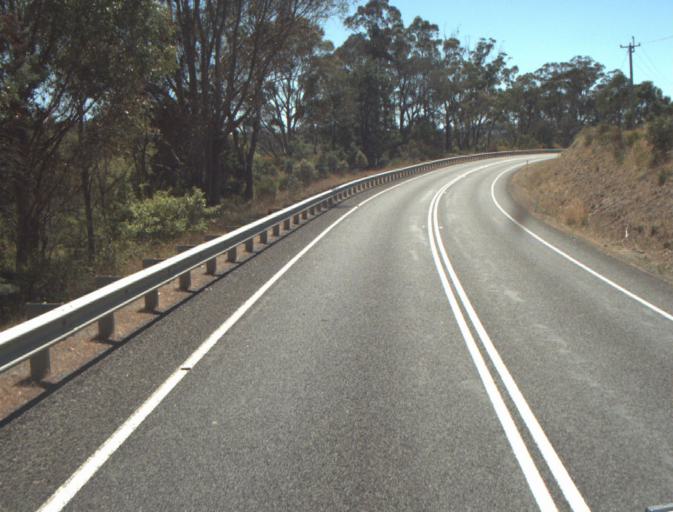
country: AU
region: Tasmania
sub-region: Launceston
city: Newstead
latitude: -41.3739
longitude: 147.3137
